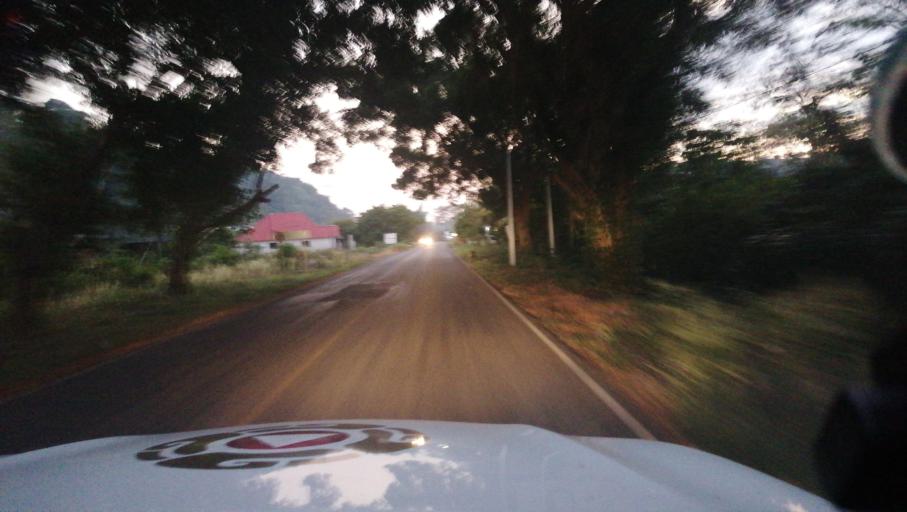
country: MX
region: Chiapas
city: Veinte de Noviembre
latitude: 14.9808
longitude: -92.2446
